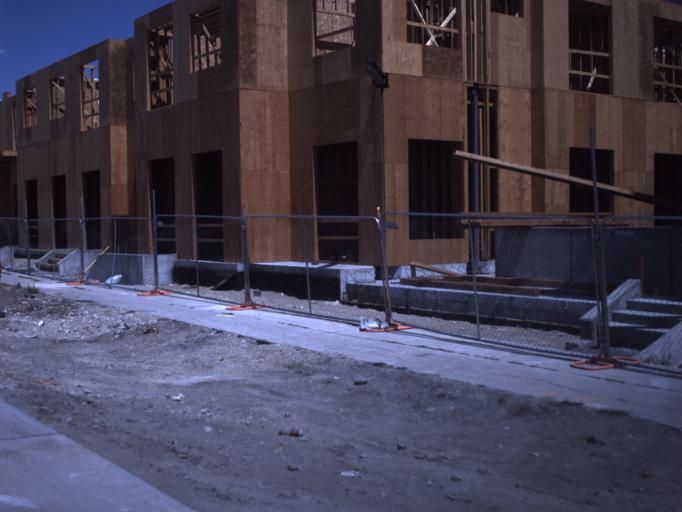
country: US
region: Utah
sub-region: Utah County
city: Provo
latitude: 40.2303
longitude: -111.6586
